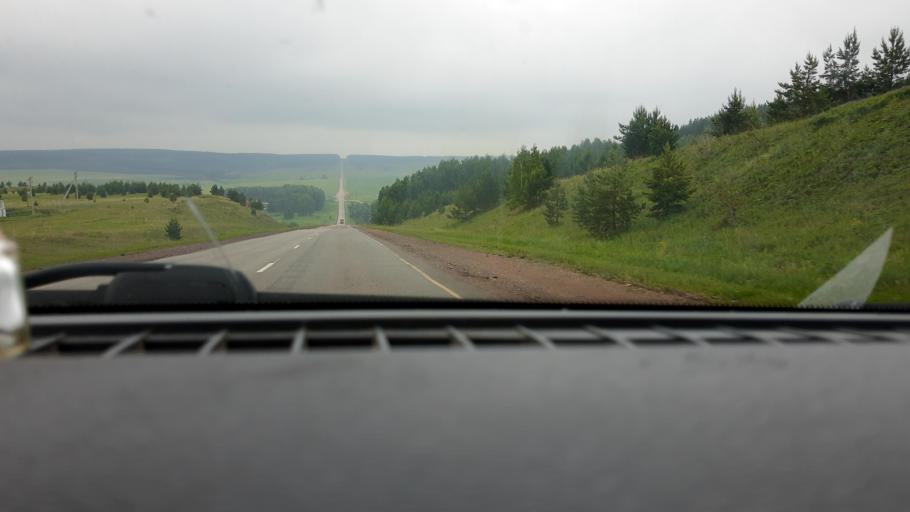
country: RU
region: Bashkortostan
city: Belebey
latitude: 54.2615
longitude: 54.0691
